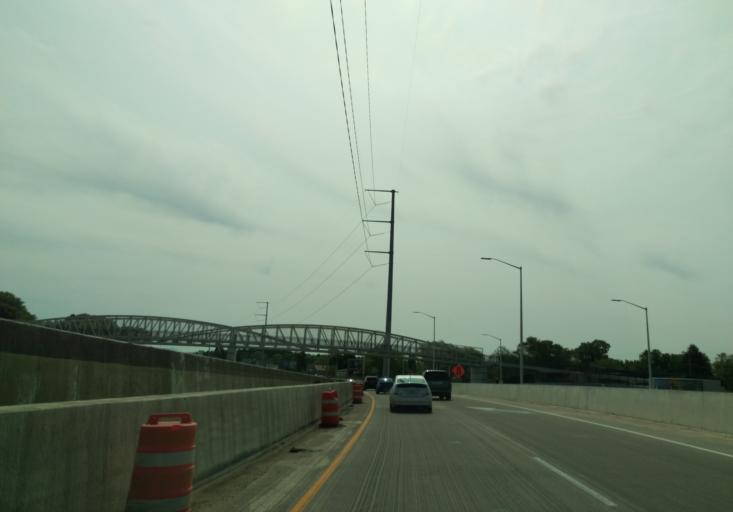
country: US
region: Wisconsin
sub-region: Dane County
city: Shorewood Hills
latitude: 43.0352
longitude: -89.4503
